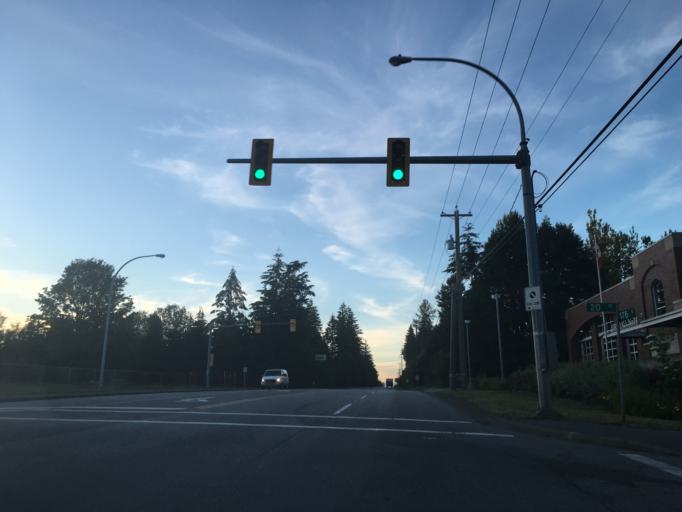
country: US
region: Washington
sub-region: Whatcom County
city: Blaine
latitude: 49.0383
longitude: -122.7351
